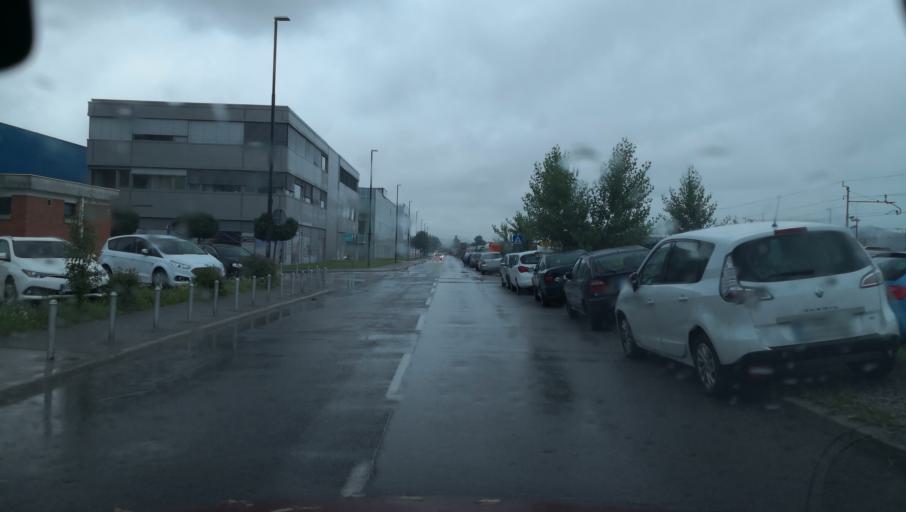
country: SI
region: Ljubljana
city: Ljubljana
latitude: 46.0846
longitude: 14.4828
